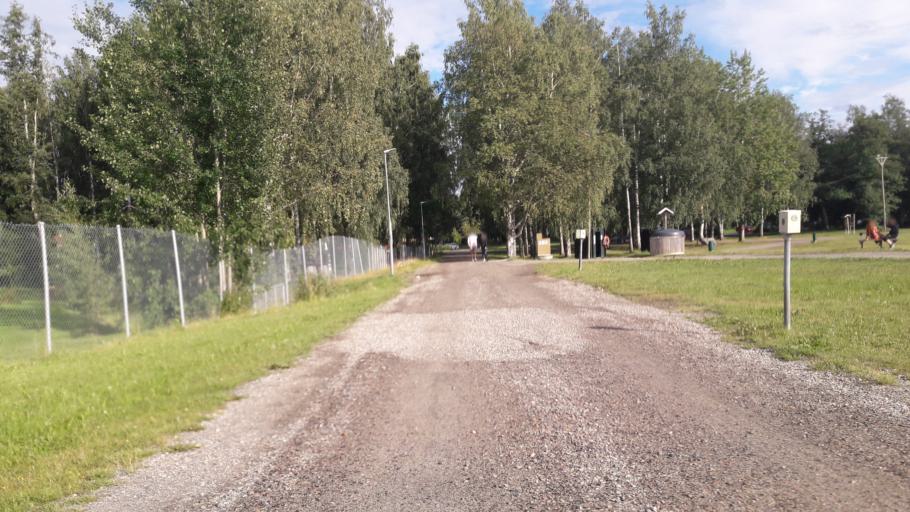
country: FI
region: North Karelia
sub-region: Joensuu
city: Joensuu
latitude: 62.5955
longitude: 29.7395
